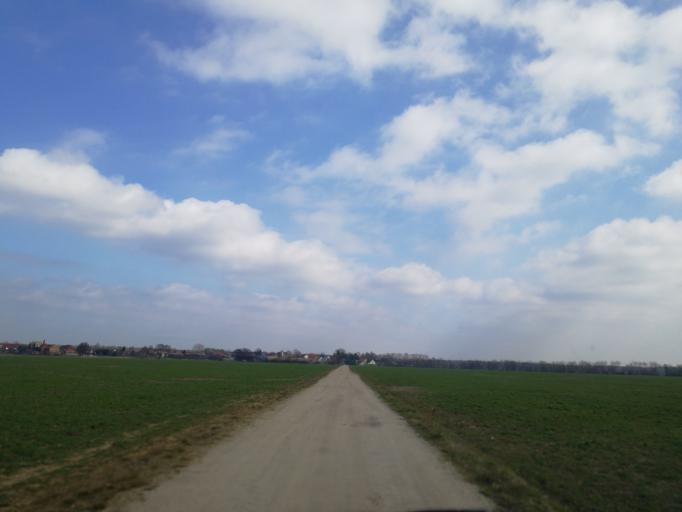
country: DE
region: Brandenburg
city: Finsterwalde
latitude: 51.6594
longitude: 13.7283
